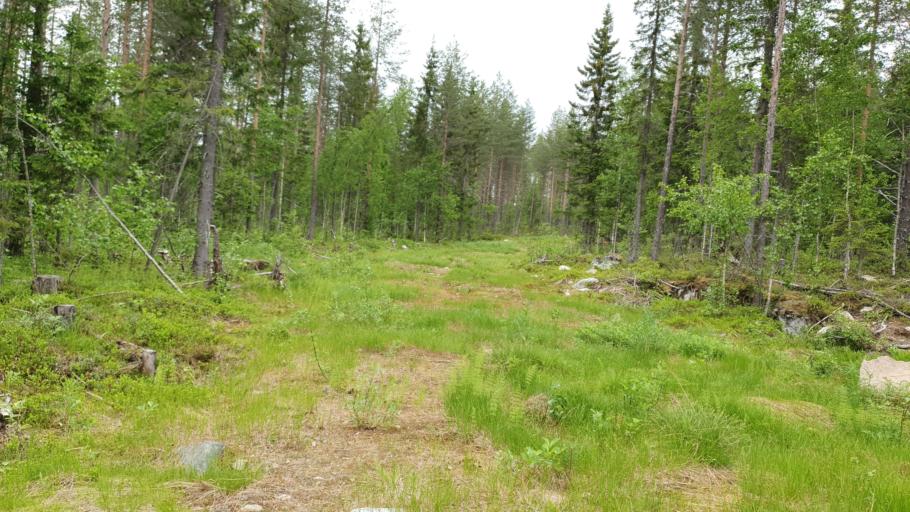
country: FI
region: Kainuu
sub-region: Kehys-Kainuu
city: Kuhmo
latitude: 64.4439
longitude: 29.6839
